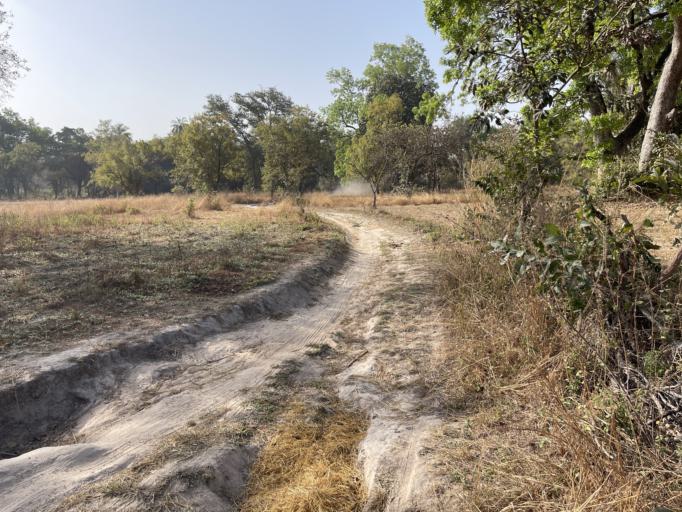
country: GW
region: Oio
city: Farim
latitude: 12.4763
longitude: -15.4069
